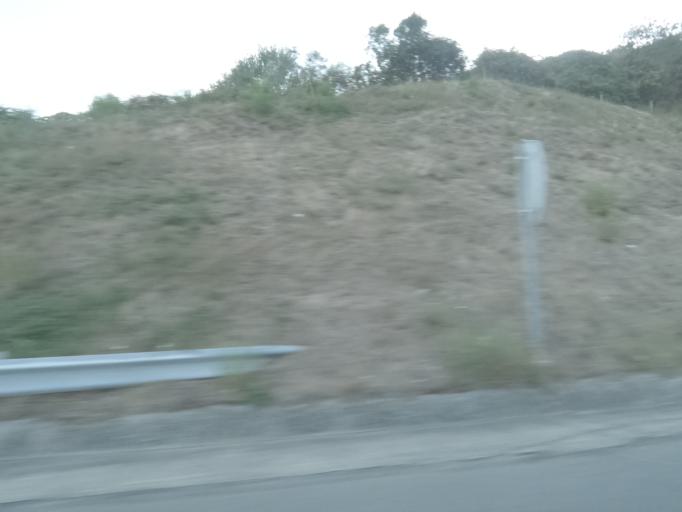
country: PT
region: Vila Real
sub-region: Peso da Regua
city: Peso da Regua
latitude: 41.1696
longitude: -7.7754
